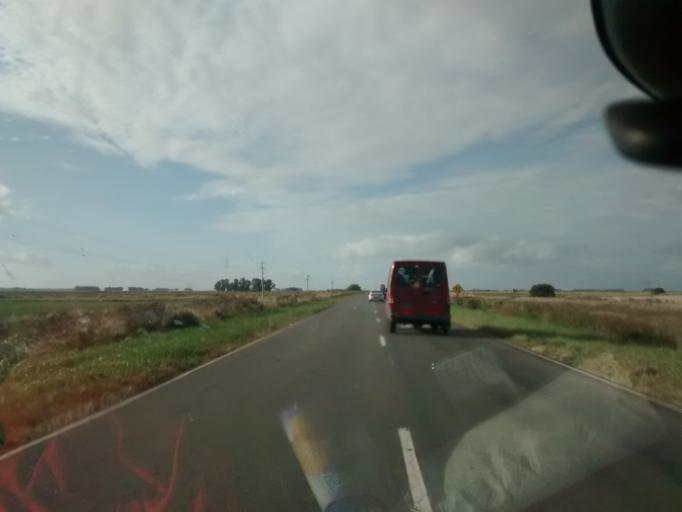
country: AR
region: Buenos Aires
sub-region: Partido de Ayacucho
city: Ayacucho
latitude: -36.8125
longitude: -58.5658
